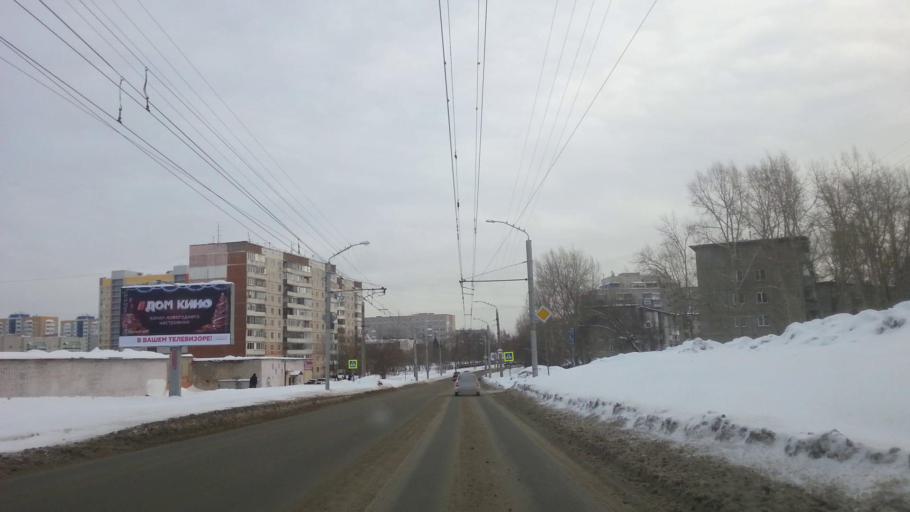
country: RU
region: Altai Krai
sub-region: Gorod Barnaulskiy
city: Barnaul
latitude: 53.3693
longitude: 83.6998
